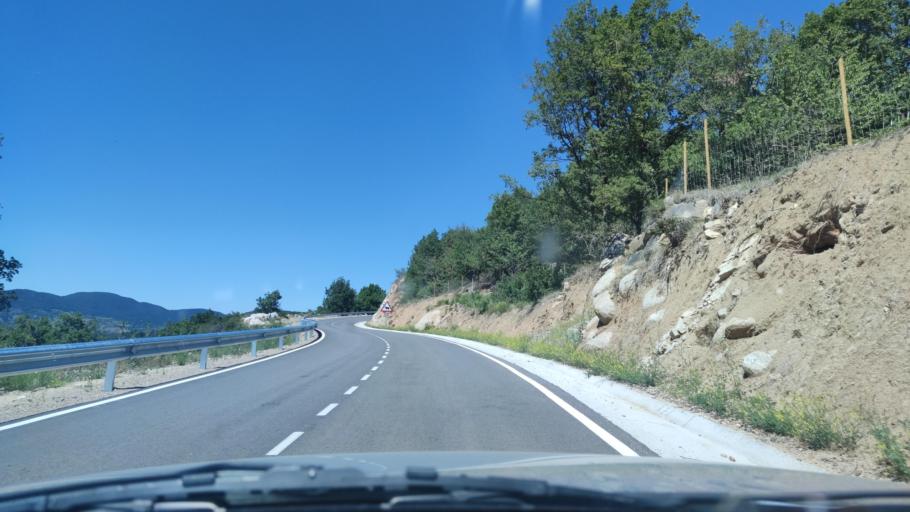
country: ES
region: Catalonia
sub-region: Provincia de Lleida
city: Lles de Cerdanya
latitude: 42.3801
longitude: 1.6891
